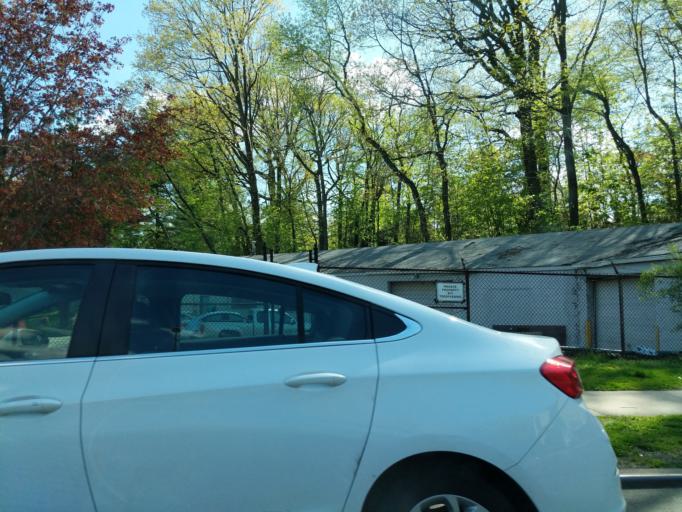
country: US
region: New York
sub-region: Queens County
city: Jamaica
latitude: 40.7115
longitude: -73.8246
